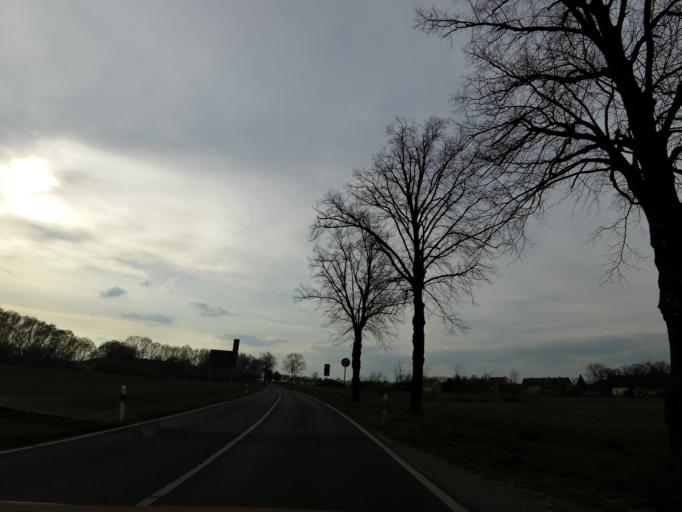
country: DE
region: Brandenburg
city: Mittenwalde
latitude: 52.3059
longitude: 13.5121
